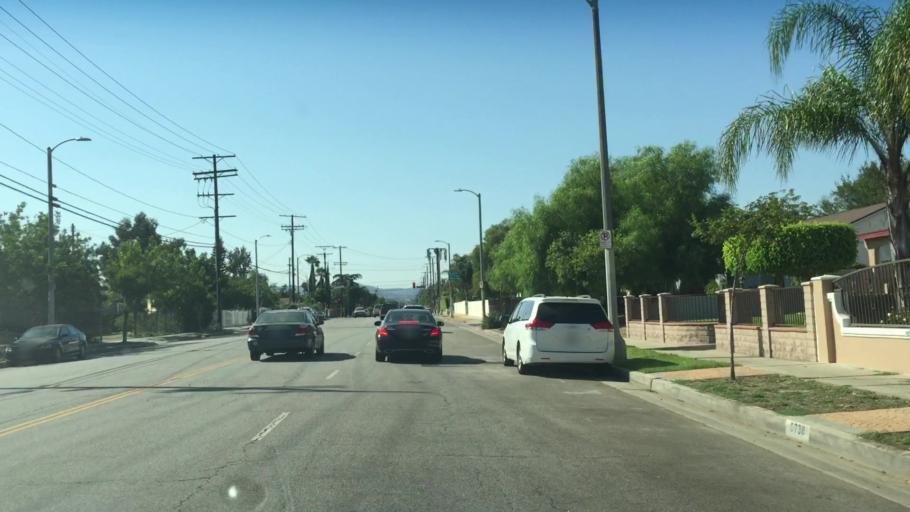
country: US
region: California
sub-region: Los Angeles County
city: San Fernando
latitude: 34.2469
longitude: -118.4310
